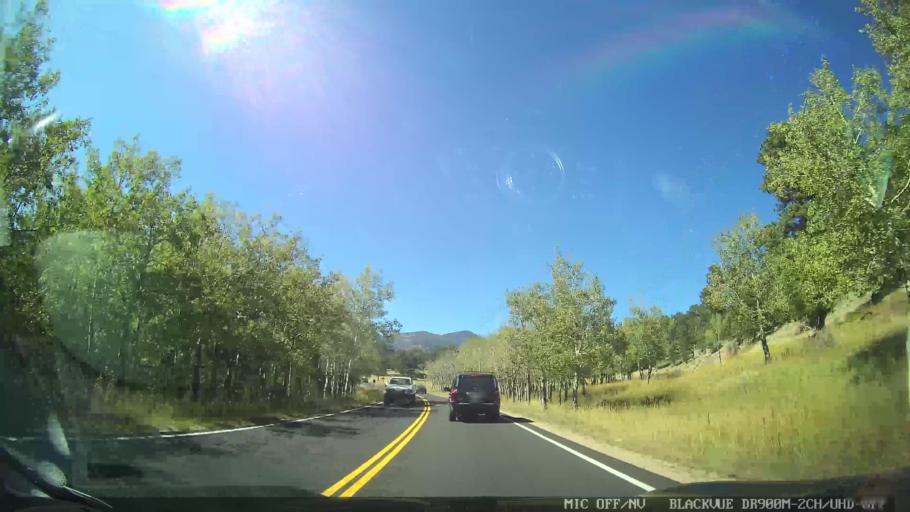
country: US
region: Colorado
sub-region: Larimer County
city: Estes Park
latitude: 40.3590
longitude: -105.5862
